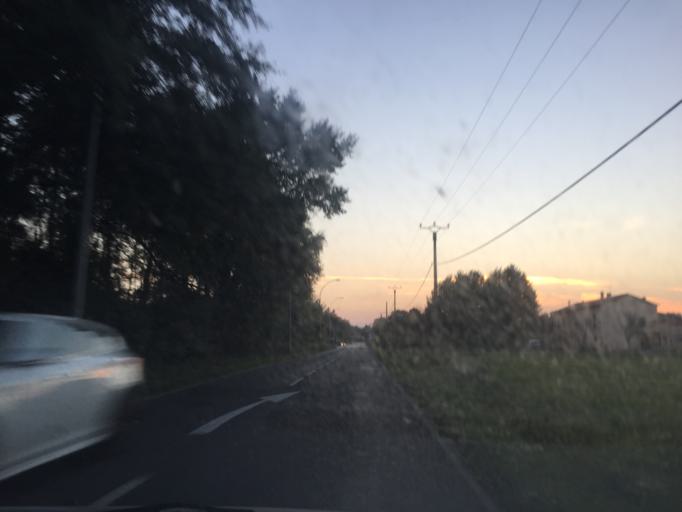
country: FR
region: Rhone-Alpes
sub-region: Departement de l'Ain
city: Mionnay
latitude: 45.8716
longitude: 4.9266
